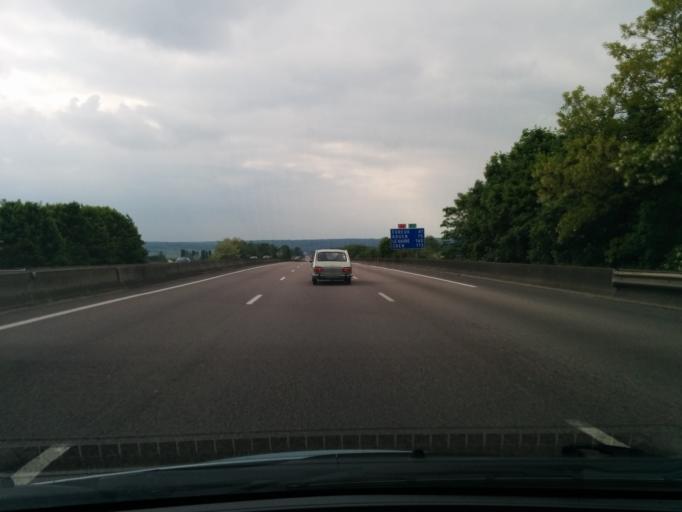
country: FR
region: Ile-de-France
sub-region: Departement des Yvelines
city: Buchelay
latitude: 48.9854
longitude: 1.6724
